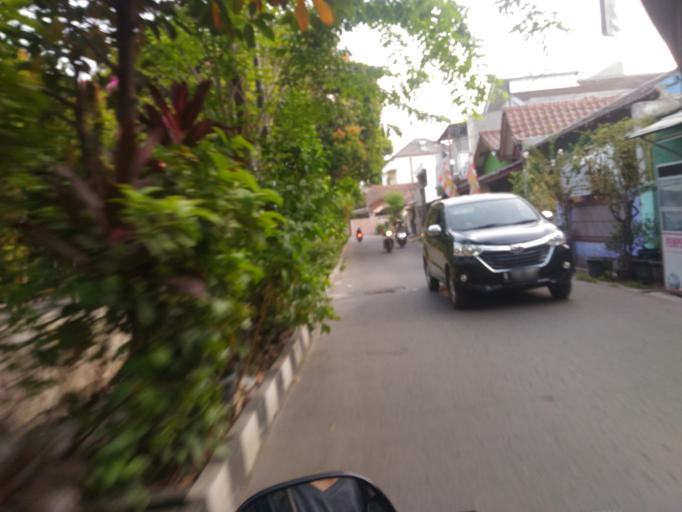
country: ID
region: West Java
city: Depok
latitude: -6.3673
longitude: 106.8546
